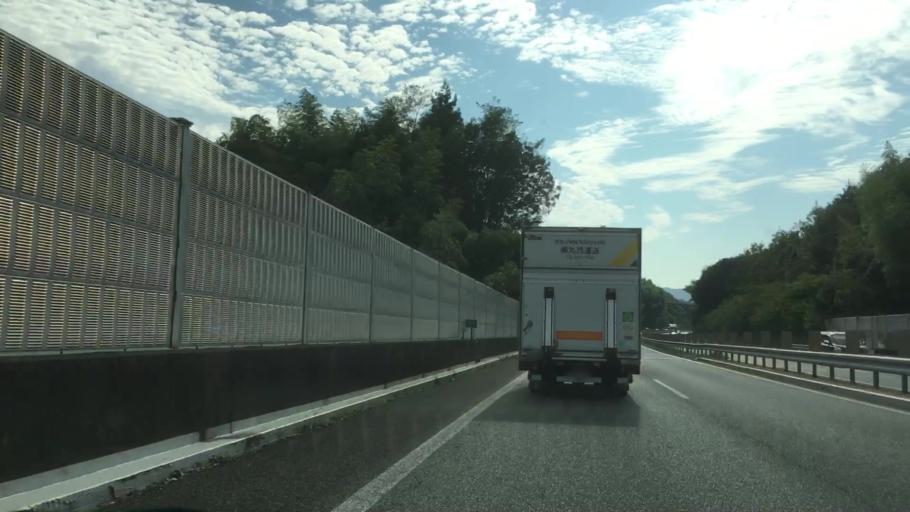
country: JP
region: Yamaguchi
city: Yanai
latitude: 34.0870
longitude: 132.0911
